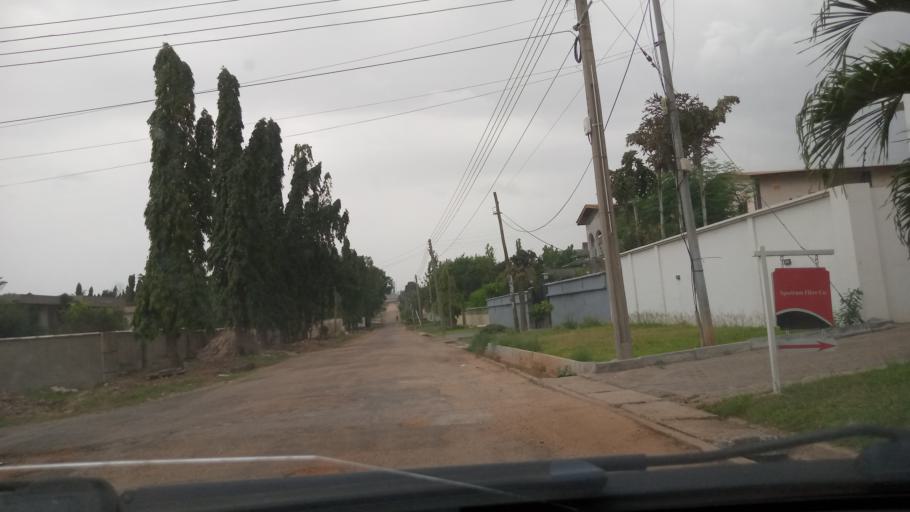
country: GH
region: Greater Accra
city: Dome
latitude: 5.6144
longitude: -0.2087
